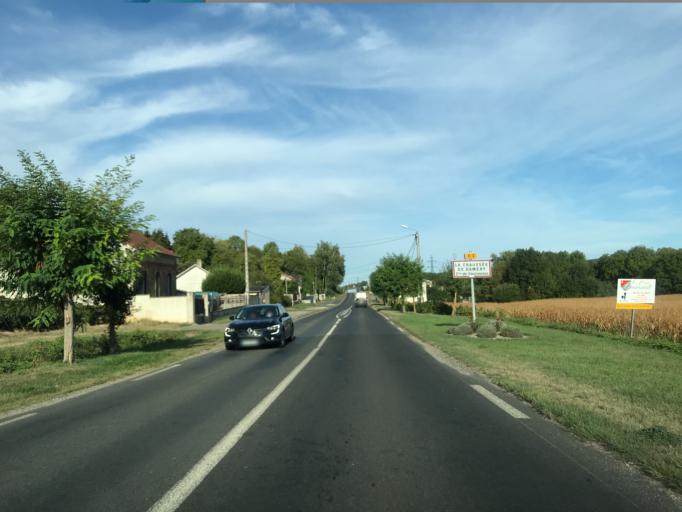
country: FR
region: Champagne-Ardenne
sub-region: Departement de la Marne
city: Damery
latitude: 49.0595
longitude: 3.8826
